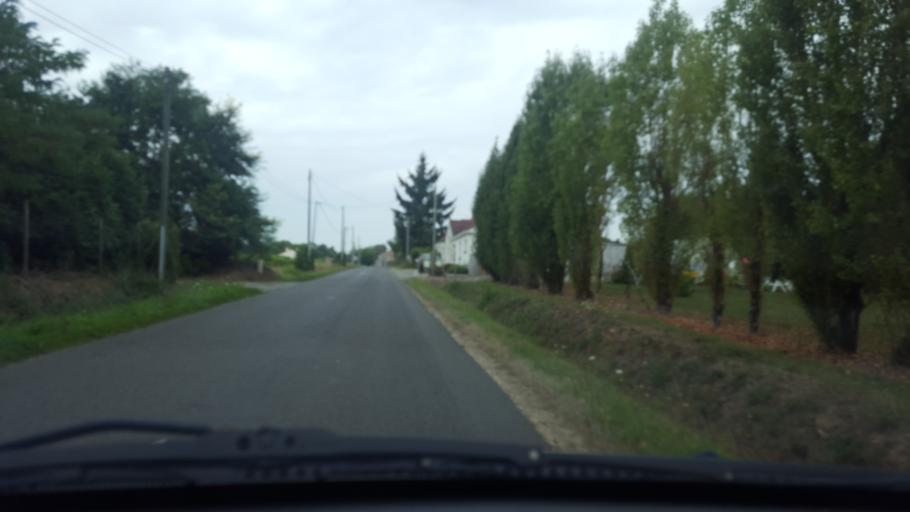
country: FR
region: Pays de la Loire
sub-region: Departement de la Loire-Atlantique
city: Saint-Philbert-de-Grand-Lieu
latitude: 46.9976
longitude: -1.6459
